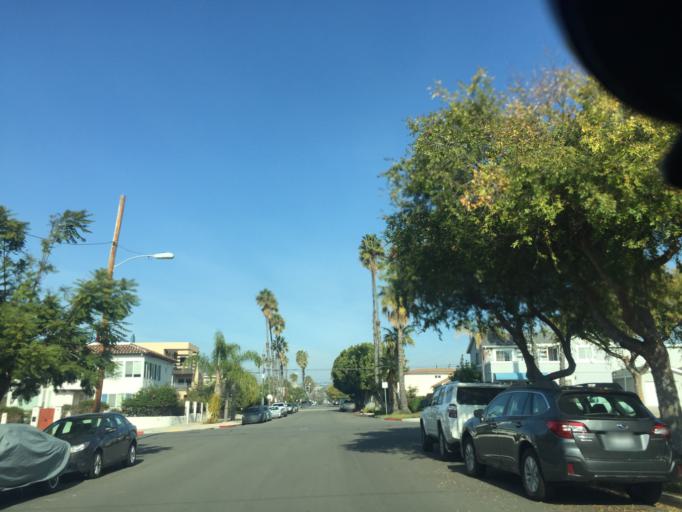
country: US
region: California
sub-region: San Diego County
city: La Jolla
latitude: 32.7930
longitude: -117.2466
